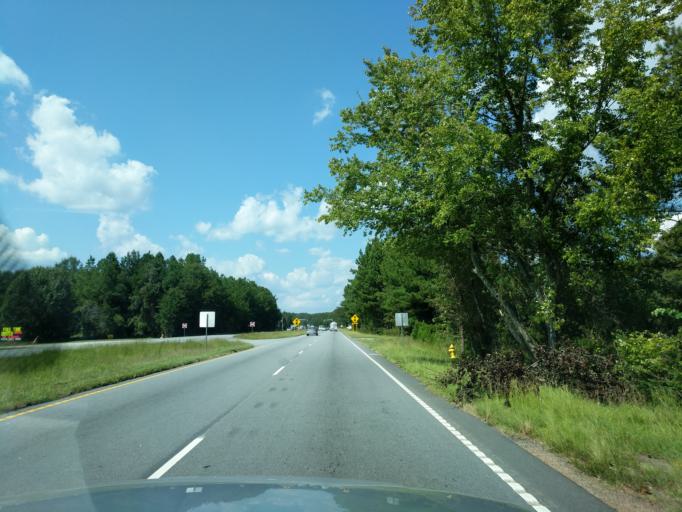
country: US
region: South Carolina
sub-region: Anderson County
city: Powdersville
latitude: 34.8008
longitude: -82.5107
